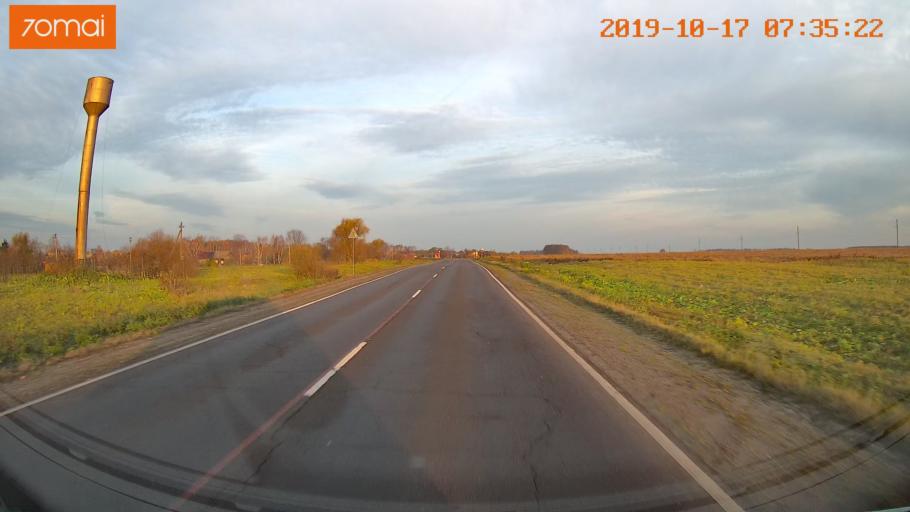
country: RU
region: Ivanovo
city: Gavrilov Posad
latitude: 56.4271
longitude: 39.9297
